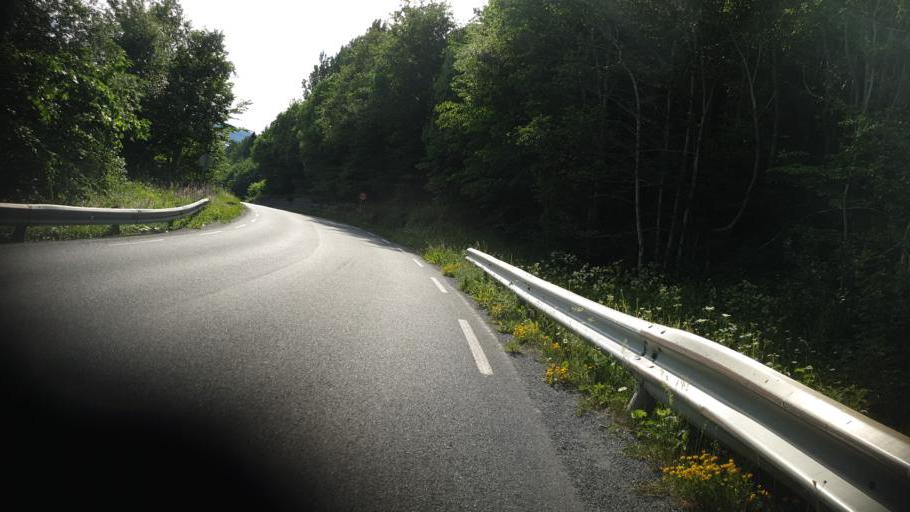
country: NO
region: Sor-Trondelag
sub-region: Trondheim
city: Trondheim
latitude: 63.5573
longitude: 10.2436
